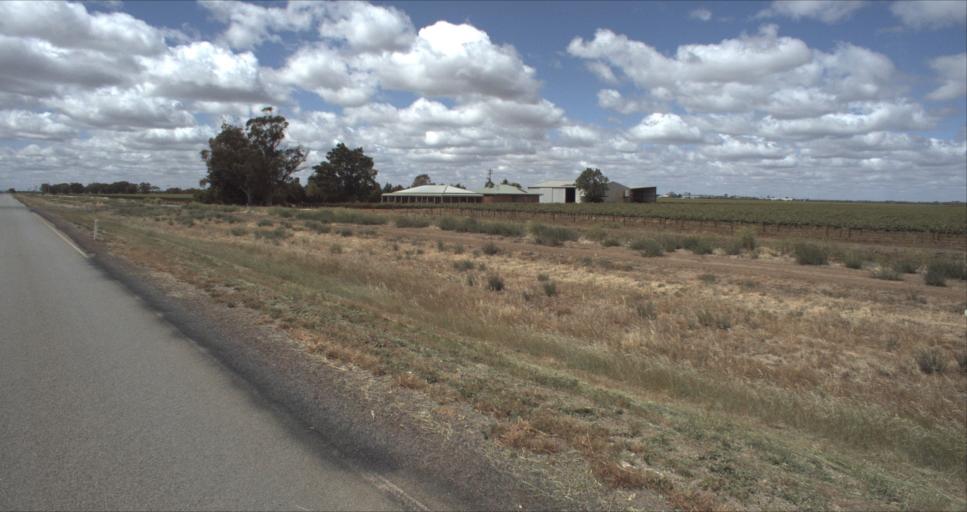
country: AU
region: New South Wales
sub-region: Murrumbidgee Shire
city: Darlington Point
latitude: -34.4952
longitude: 146.1736
